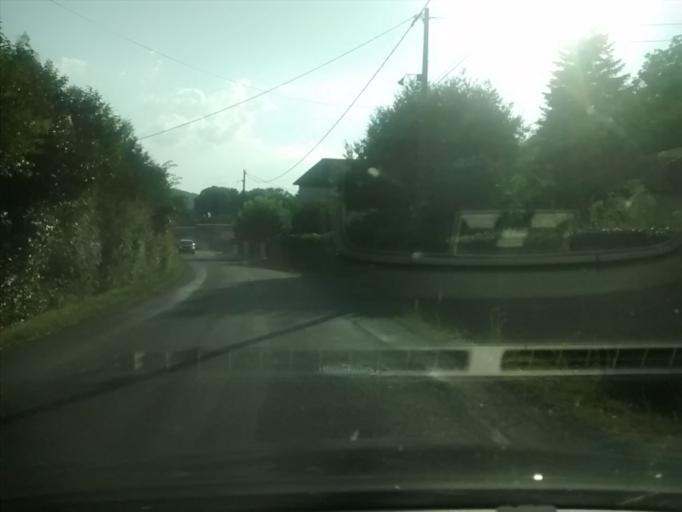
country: FR
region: Aquitaine
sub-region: Departement de la Dordogne
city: Lalinde
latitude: 44.8407
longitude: 0.7440
